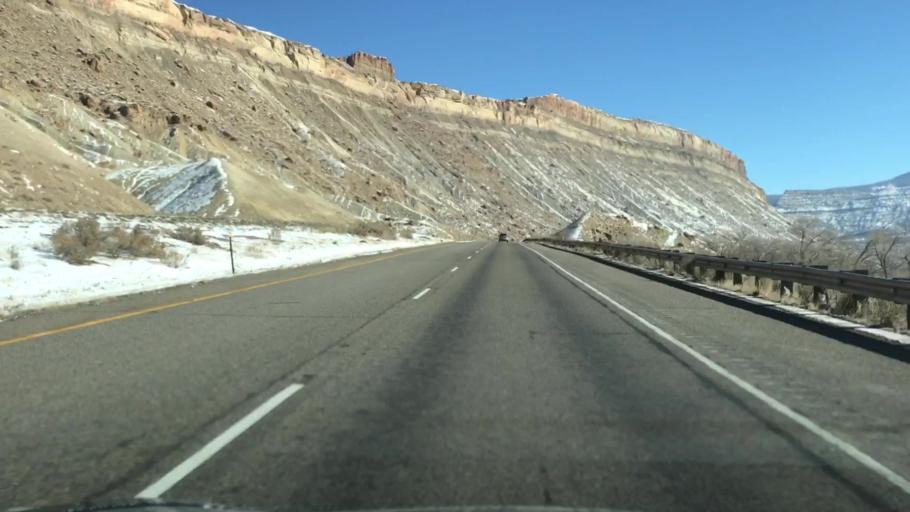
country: US
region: Colorado
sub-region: Mesa County
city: Palisade
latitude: 39.1194
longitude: -108.3800
